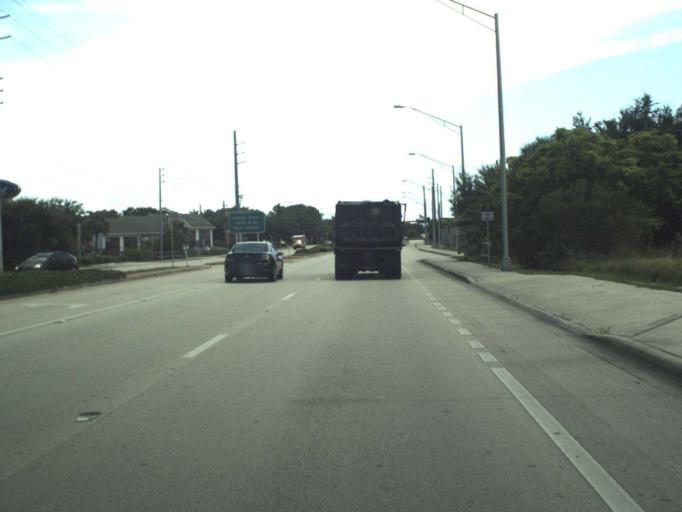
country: US
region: Florida
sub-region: Indian River County
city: Vero Beach South
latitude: 27.6111
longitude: -80.3852
